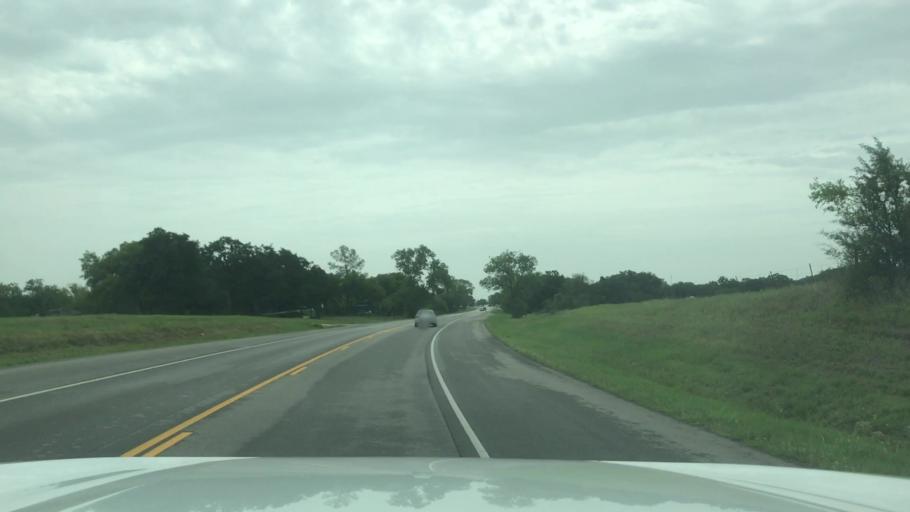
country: US
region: Texas
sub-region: Eastland County
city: Gorman
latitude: 32.2209
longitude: -98.6794
